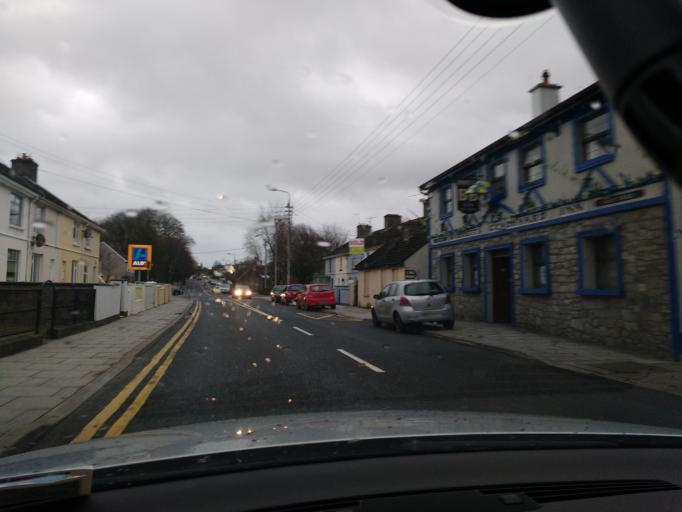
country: IE
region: Munster
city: Thurles
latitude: 52.6798
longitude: -7.8021
